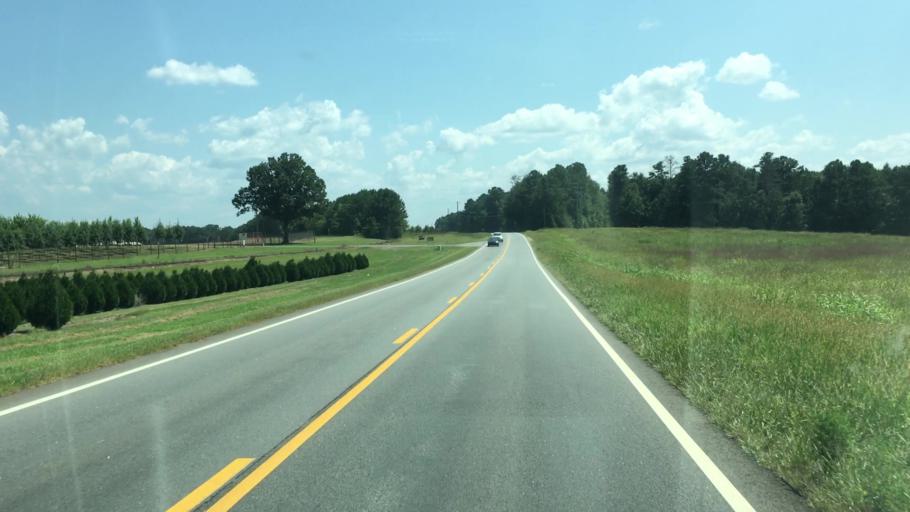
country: US
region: Georgia
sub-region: Oconee County
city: Watkinsville
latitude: 33.7528
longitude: -83.4351
